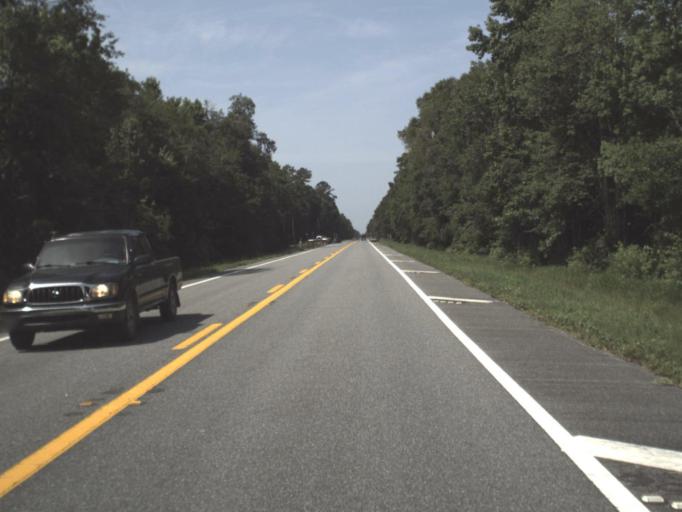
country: US
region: Florida
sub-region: Taylor County
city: Steinhatchee
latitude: 29.8464
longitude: -83.3110
